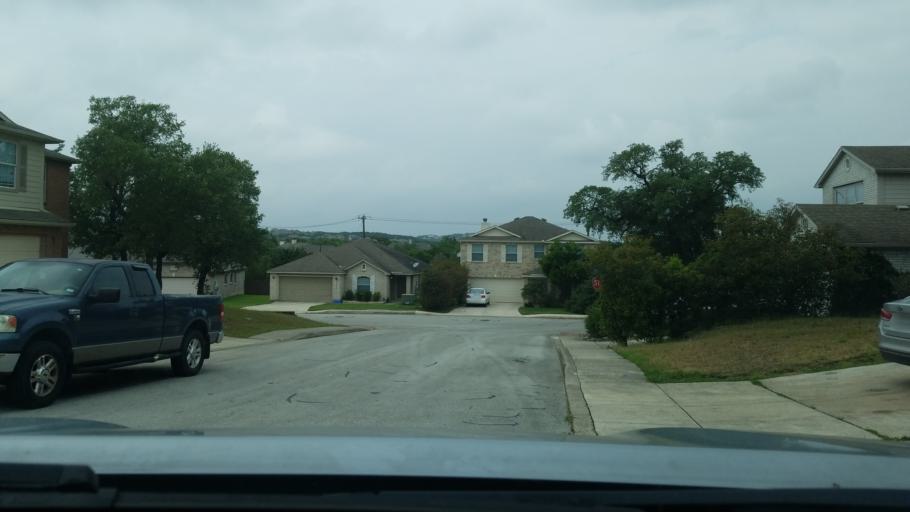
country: US
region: Texas
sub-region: Bexar County
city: Timberwood Park
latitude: 29.6811
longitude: -98.4676
